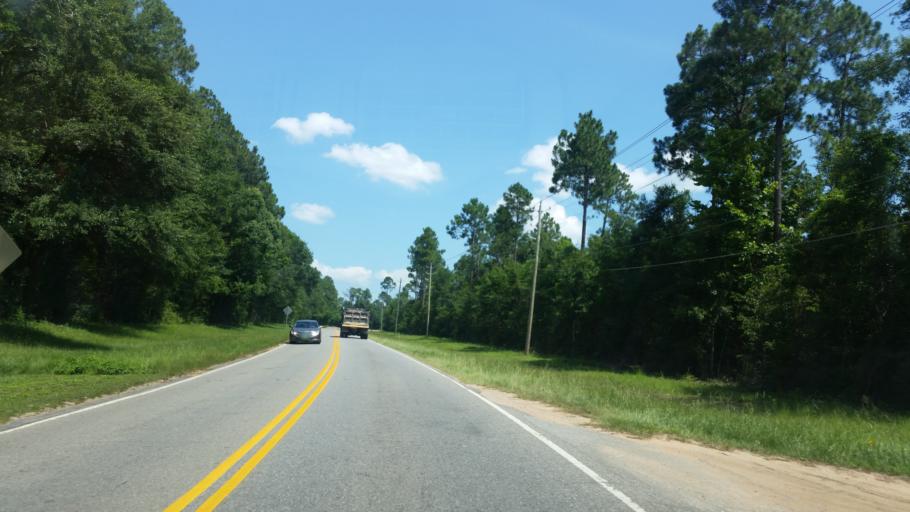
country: US
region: Florida
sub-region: Escambia County
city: Cantonment
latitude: 30.6031
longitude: -87.3313
